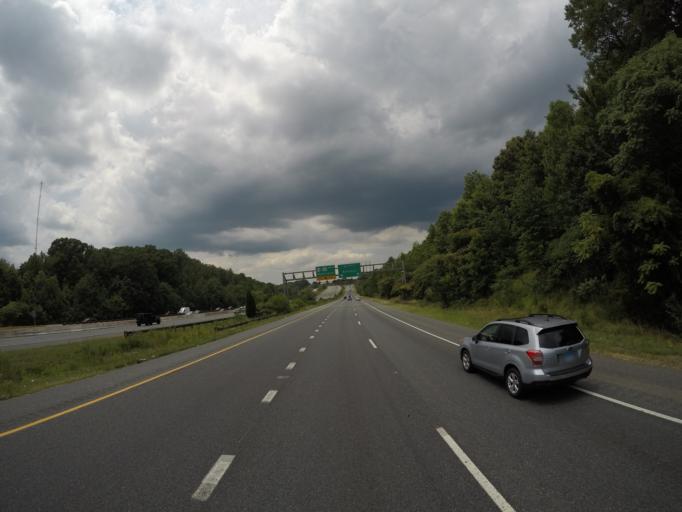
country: US
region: Maryland
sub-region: Anne Arundel County
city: Edgewater
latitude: 38.9837
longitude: -76.5626
